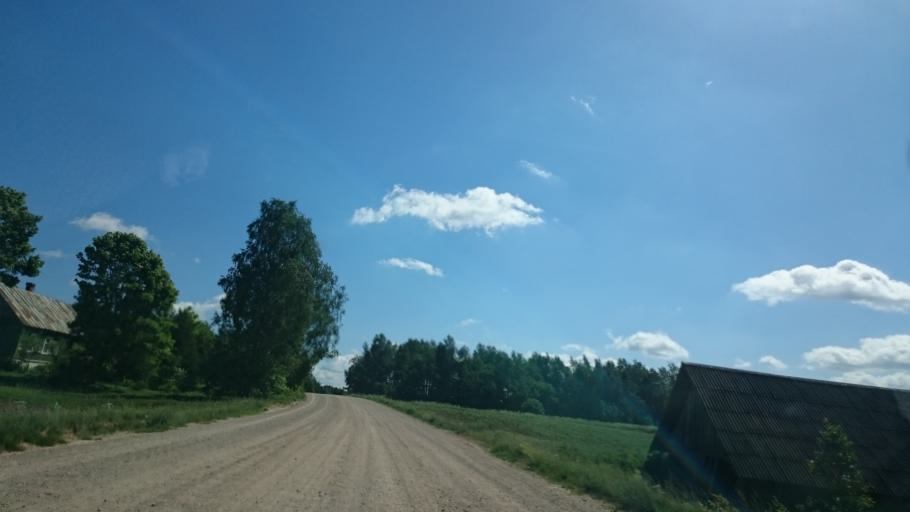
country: LV
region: Cibla
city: Cibla
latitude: 56.5354
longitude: 27.9024
